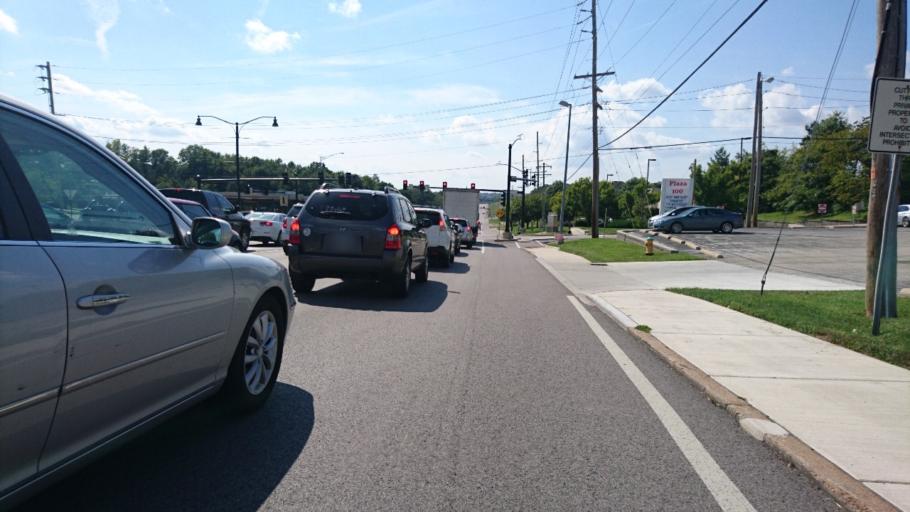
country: US
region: Missouri
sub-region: Saint Louis County
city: Ellisville
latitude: 38.5909
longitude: -90.5946
